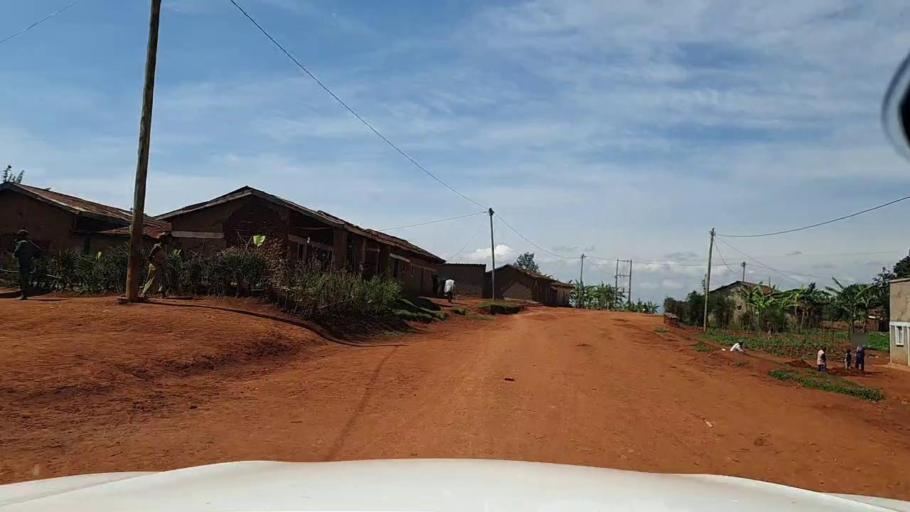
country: RW
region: Southern Province
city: Butare
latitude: -2.7206
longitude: 29.8373
